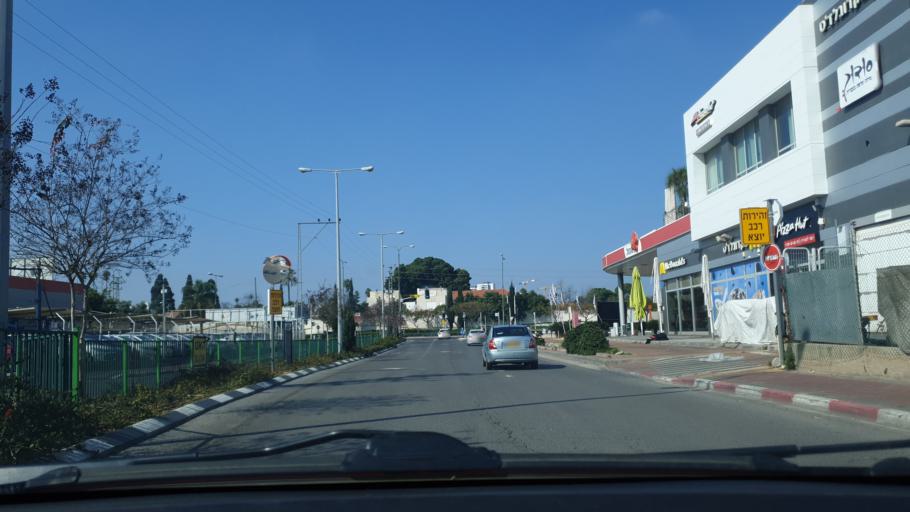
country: IL
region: Central District
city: Rishon LeZiyyon
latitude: 31.9764
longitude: 34.8090
